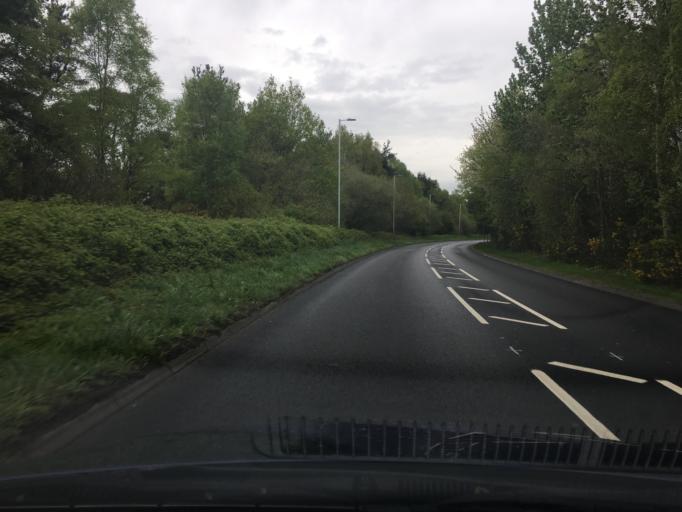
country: GB
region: England
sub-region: Bracknell Forest
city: Sandhurst
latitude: 51.3537
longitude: -0.7883
